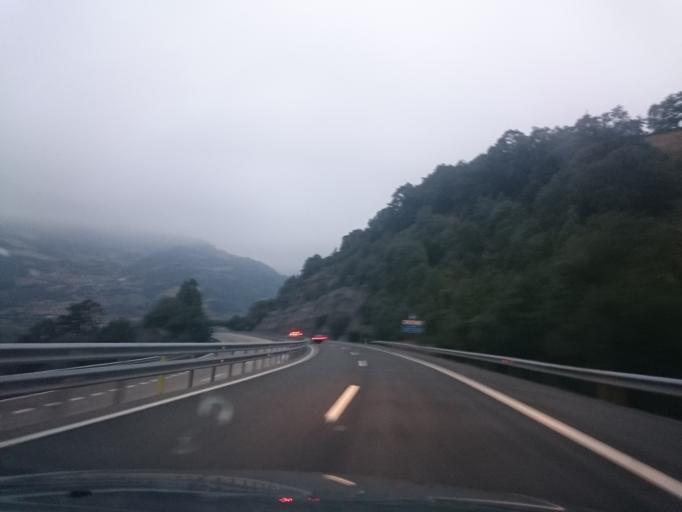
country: ES
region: Asturias
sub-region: Province of Asturias
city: Pola de Lena
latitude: 43.0553
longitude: -5.8206
